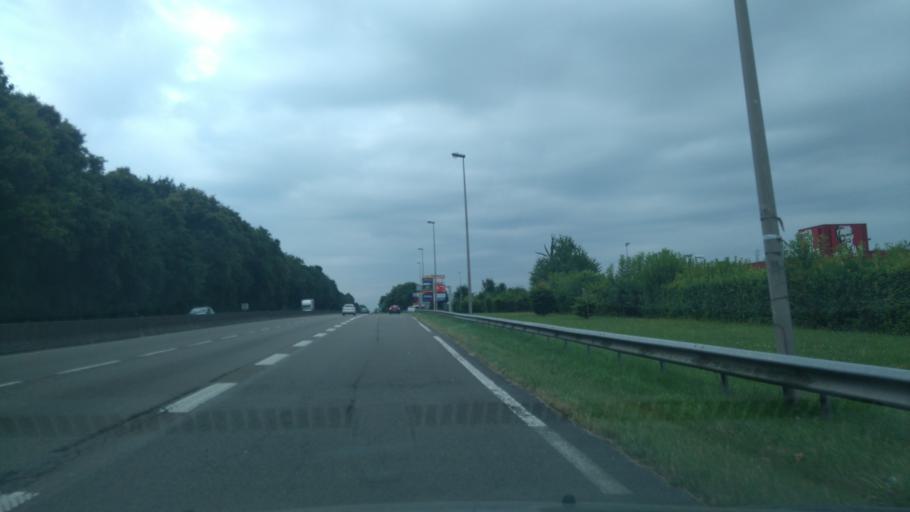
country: FR
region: Picardie
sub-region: Departement de l'Oise
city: Creil
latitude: 49.2414
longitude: 2.4737
